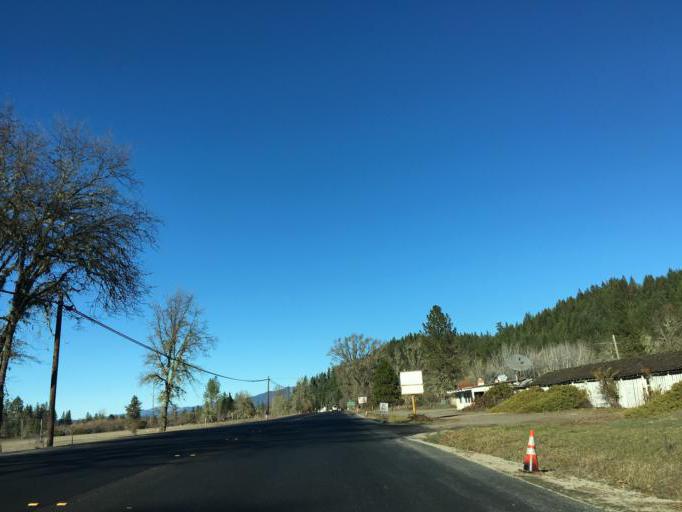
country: US
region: California
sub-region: Mendocino County
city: Laytonville
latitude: 39.6484
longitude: -123.4763
